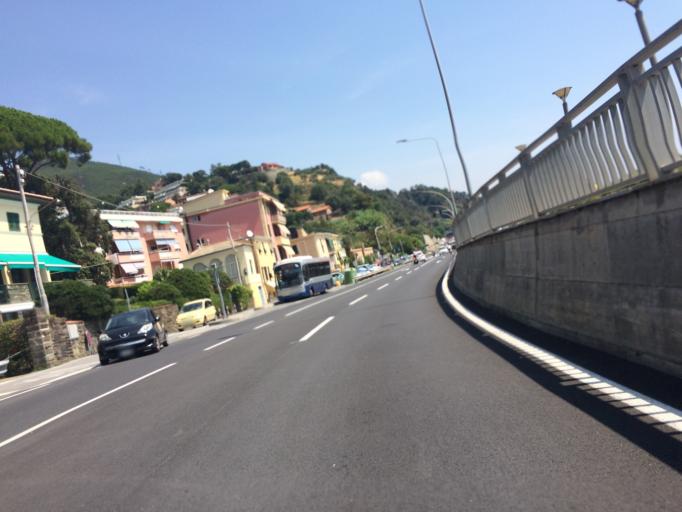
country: IT
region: Liguria
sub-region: Provincia di Genova
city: Arenzano
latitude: 44.4065
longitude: 8.6891
